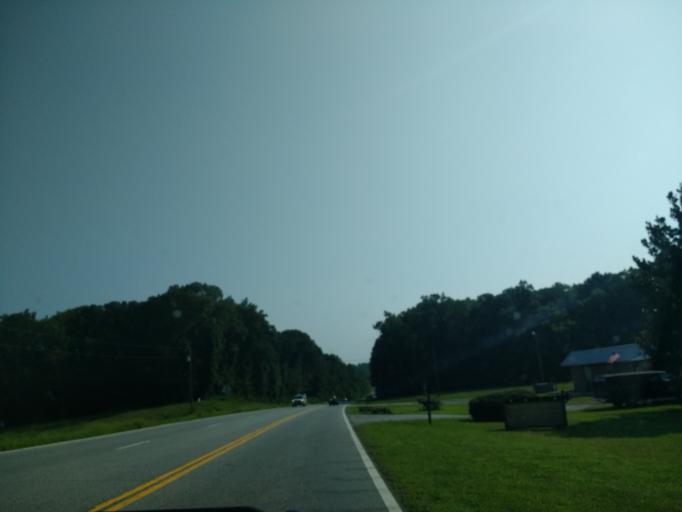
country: US
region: Georgia
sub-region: White County
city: Cleveland
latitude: 34.4528
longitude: -83.8017
